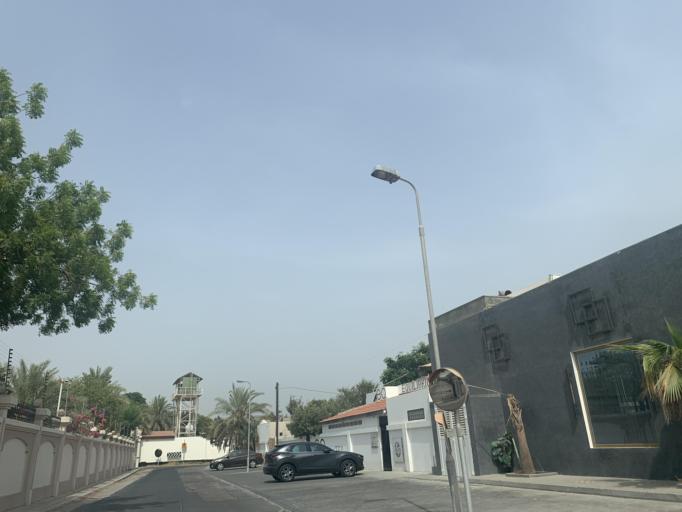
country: BH
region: Manama
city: Jidd Hafs
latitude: 26.1989
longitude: 50.4766
